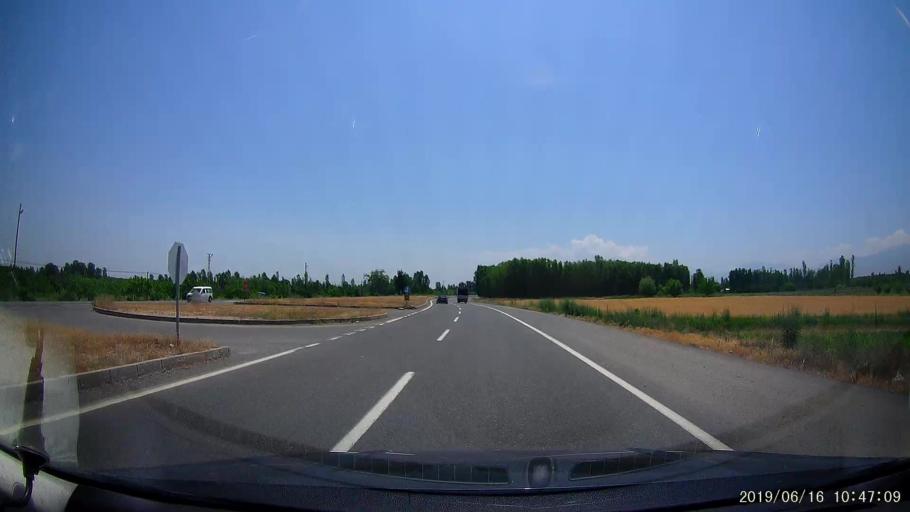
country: AM
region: Armavir
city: Shenavan
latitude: 40.0144
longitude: 43.8858
